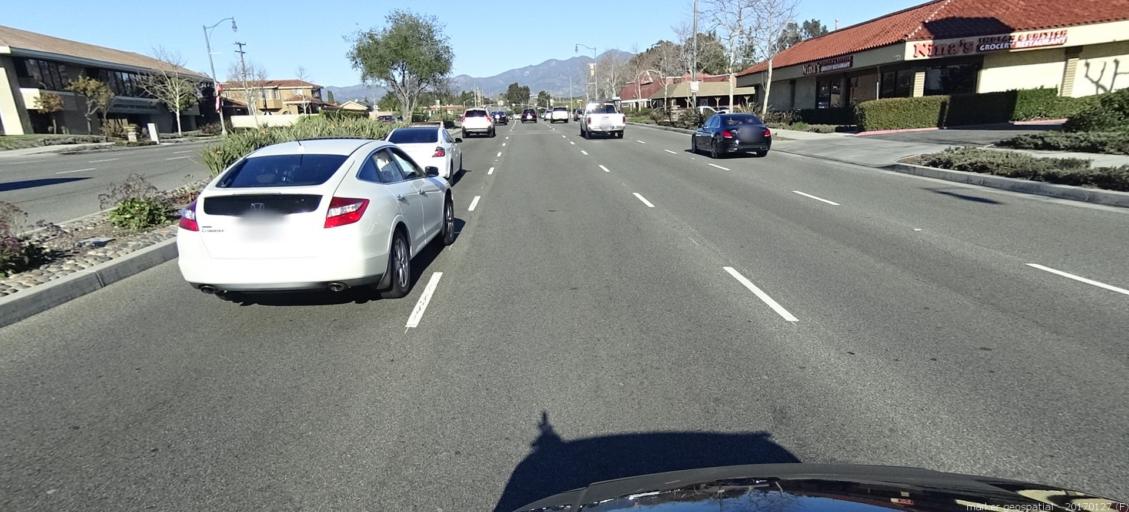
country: US
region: California
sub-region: Orange County
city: Laguna Hills
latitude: 33.6208
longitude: -117.7000
